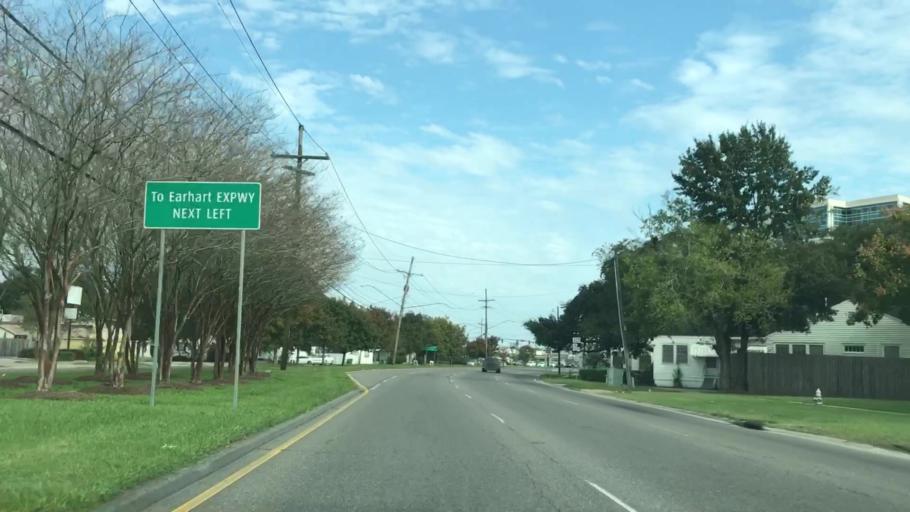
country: US
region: Louisiana
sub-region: Jefferson Parish
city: Jefferson
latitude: 29.9632
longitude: -90.1501
